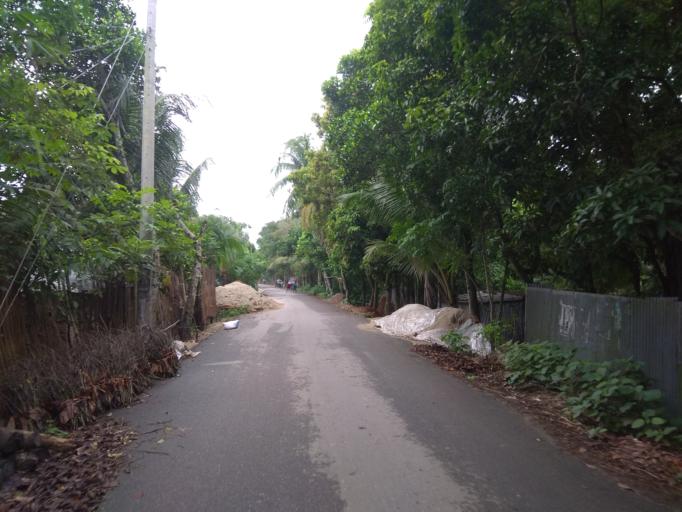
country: BD
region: Dhaka
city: Dohar
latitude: 23.4210
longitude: 90.0657
